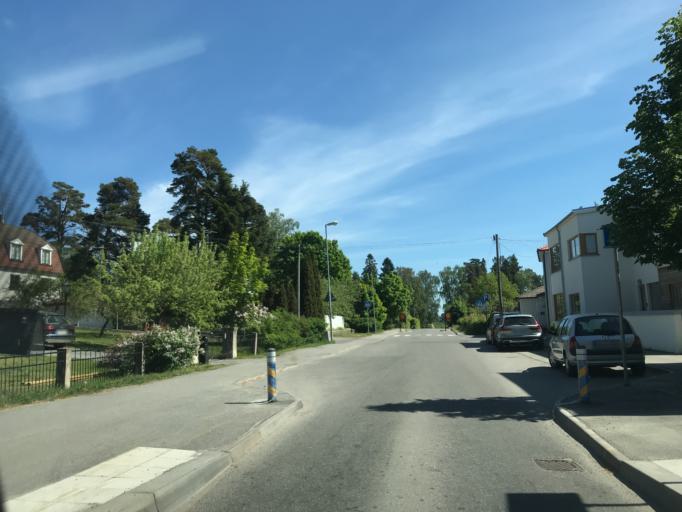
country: SE
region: Stockholm
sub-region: Sollentuna Kommun
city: Sollentuna
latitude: 59.4194
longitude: 17.9729
